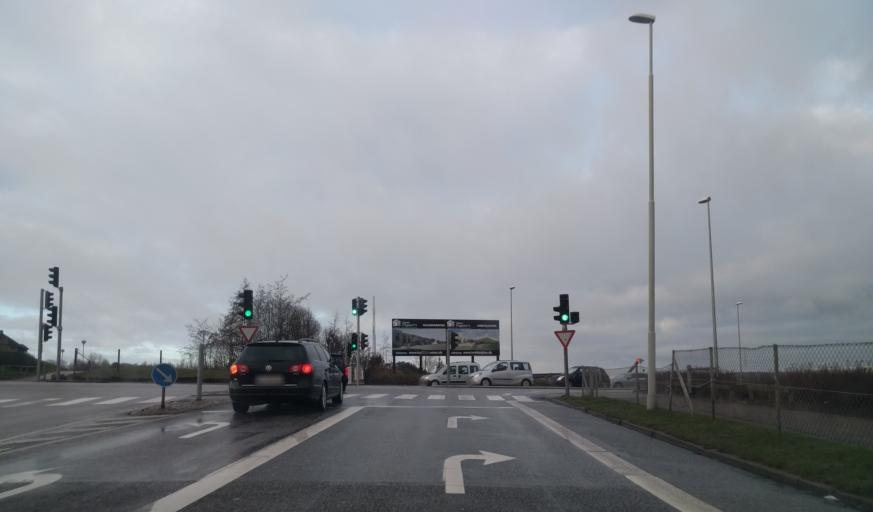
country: DK
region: North Denmark
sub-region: Alborg Kommune
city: Aalborg
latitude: 57.0329
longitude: 9.9436
